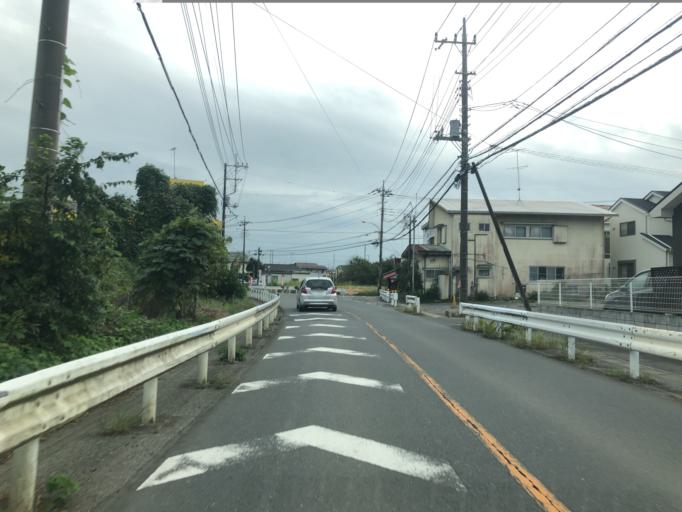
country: JP
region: Saitama
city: Fukiage-fujimi
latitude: 36.0517
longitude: 139.3953
